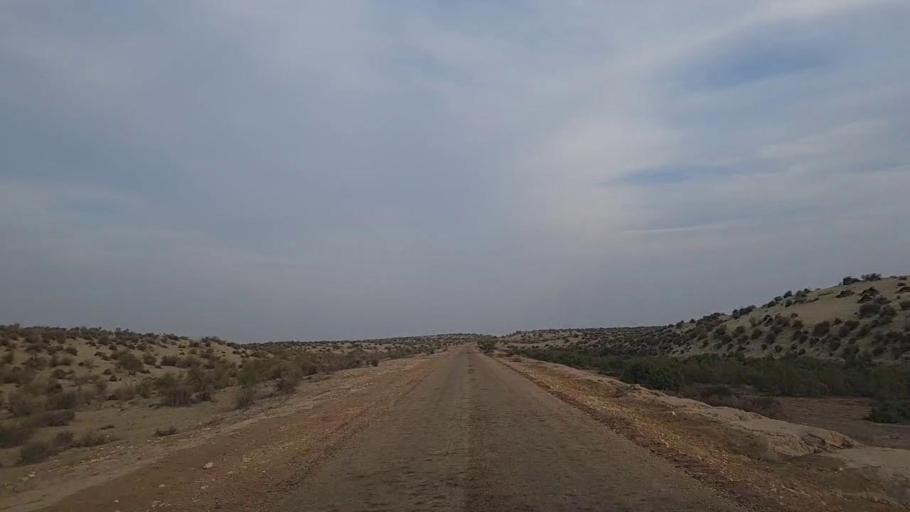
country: PK
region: Sindh
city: Jam Sahib
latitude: 26.4931
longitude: 68.5424
